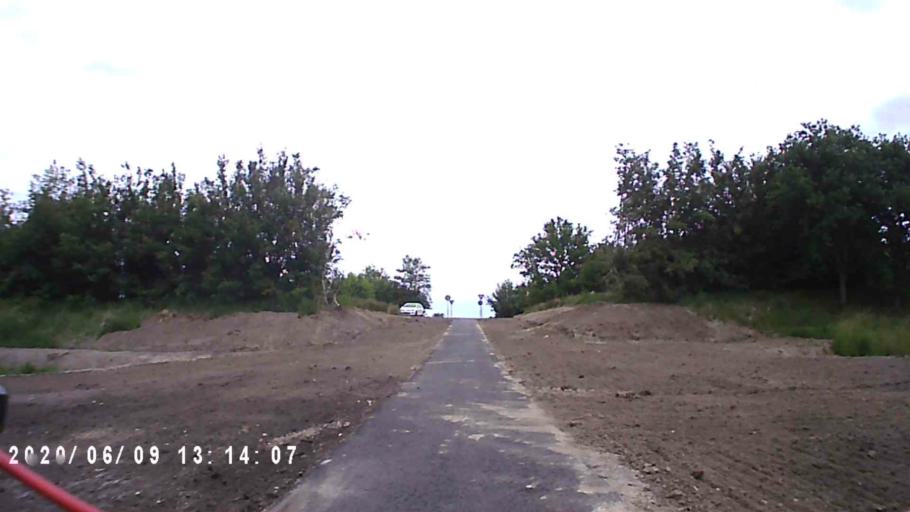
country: NL
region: Groningen
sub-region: Gemeente Haren
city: Haren
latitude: 53.2144
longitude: 6.6678
